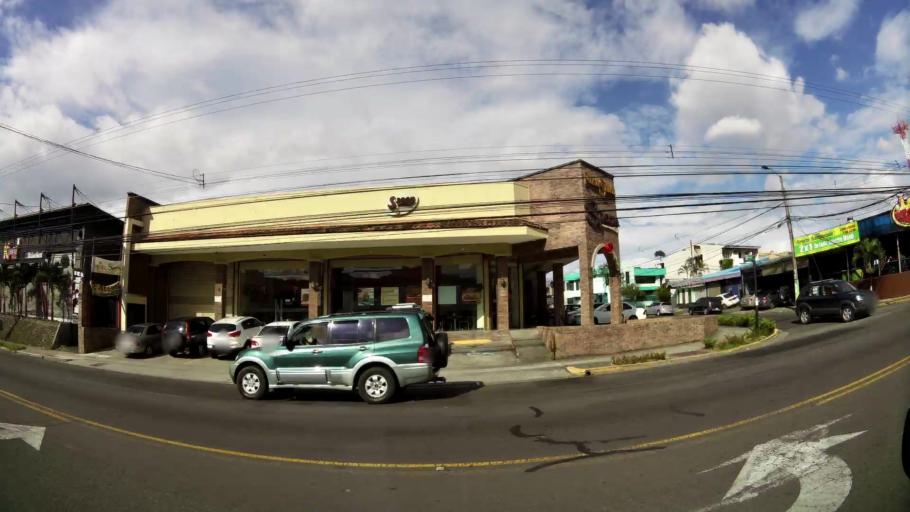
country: CR
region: San Jose
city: San Rafael
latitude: 9.9403
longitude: -84.1202
